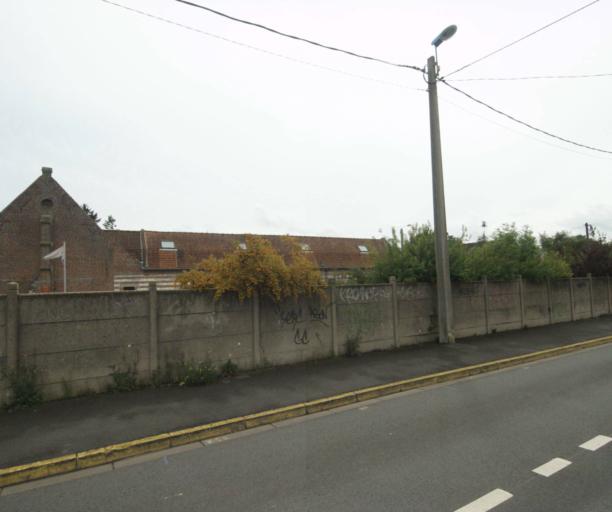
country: FR
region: Nord-Pas-de-Calais
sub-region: Departement du Nord
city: Faches-Thumesnil
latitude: 50.5904
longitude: 3.0748
